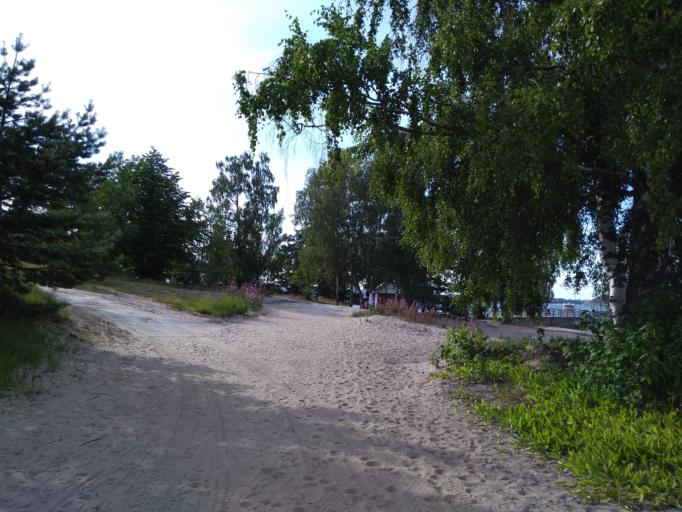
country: FI
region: Uusimaa
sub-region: Helsinki
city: Helsinki
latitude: 60.1397
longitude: 24.9170
